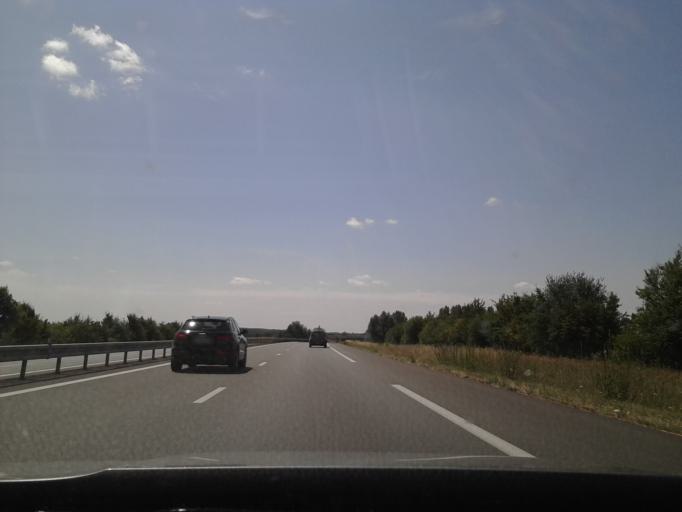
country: FR
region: Pays de la Loire
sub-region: Departement de la Sarthe
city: Brette-les-Pins
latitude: 47.9069
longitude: 0.3029
